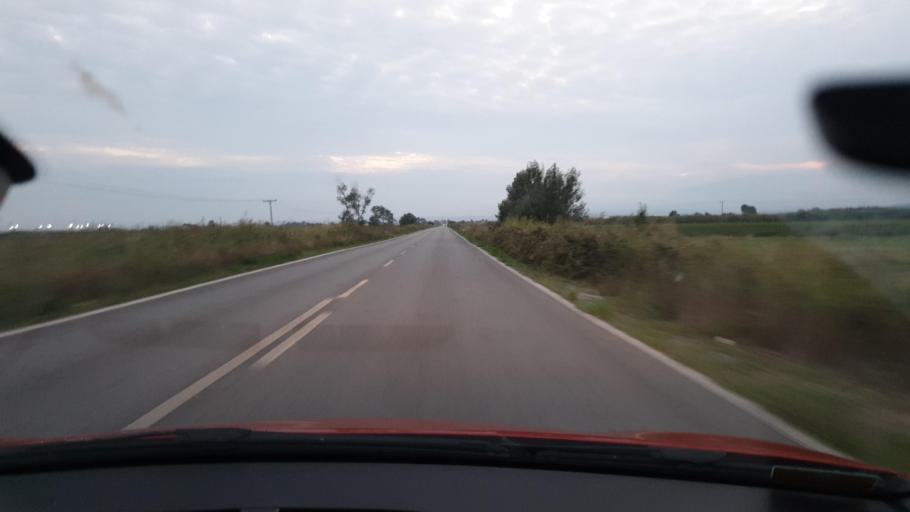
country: GR
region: Central Macedonia
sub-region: Nomos Kilkis
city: Polykastro
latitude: 41.0005
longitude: 22.6341
